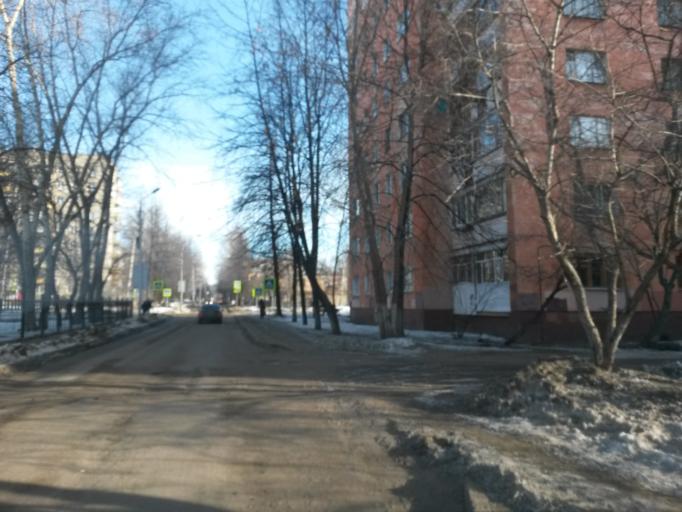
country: RU
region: Jaroslavl
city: Yaroslavl
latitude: 57.6228
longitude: 39.8533
